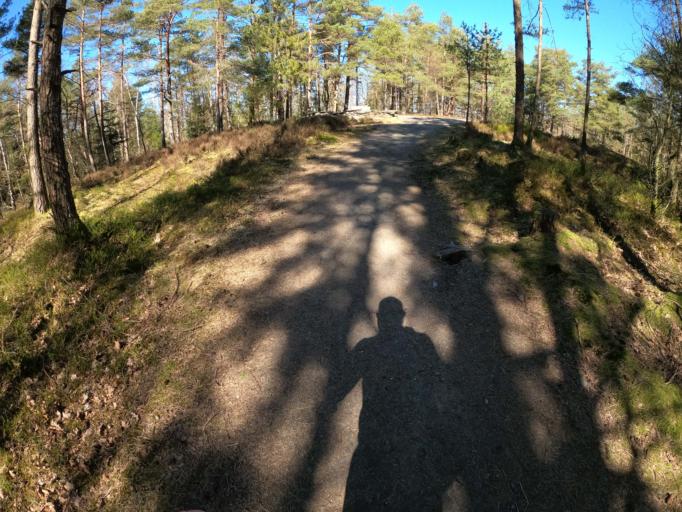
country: SE
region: Vaestra Goetaland
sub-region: Harryda Kommun
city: Molnlycke
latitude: 57.6215
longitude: 12.1107
